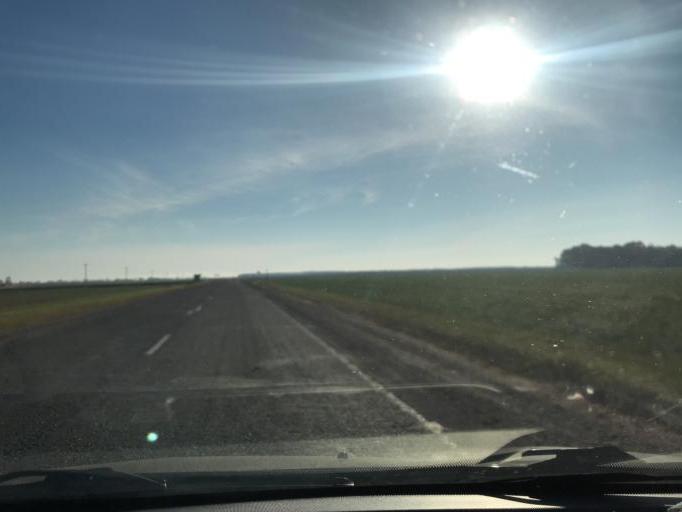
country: BY
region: Gomel
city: Brahin
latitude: 51.7930
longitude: 30.1658
